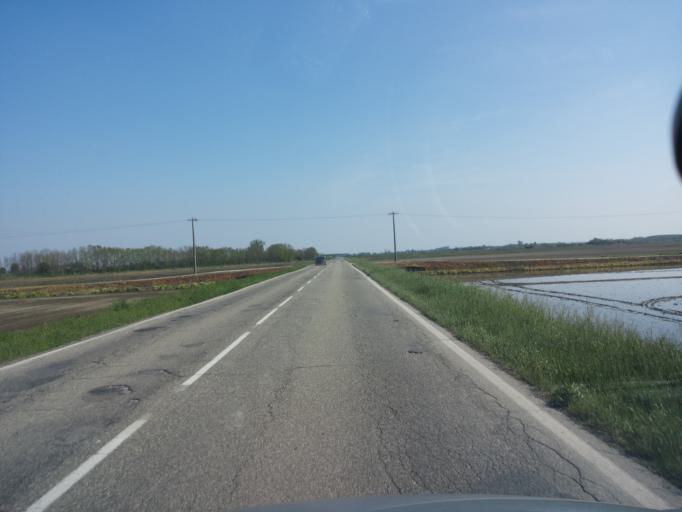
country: IT
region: Lombardy
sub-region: Provincia di Pavia
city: Langosco
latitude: 45.2079
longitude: 8.5741
